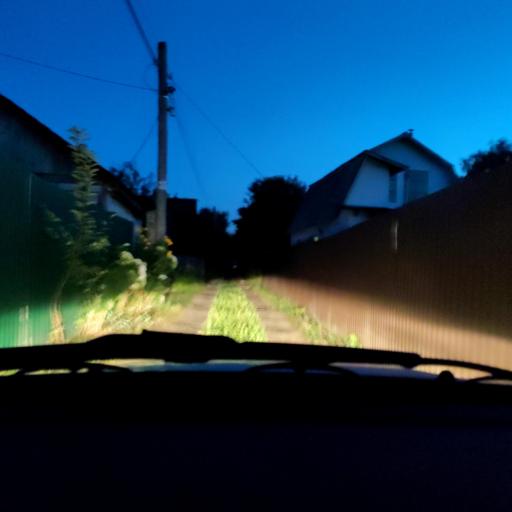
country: RU
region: Voronezj
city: Shilovo
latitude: 51.5945
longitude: 39.1487
